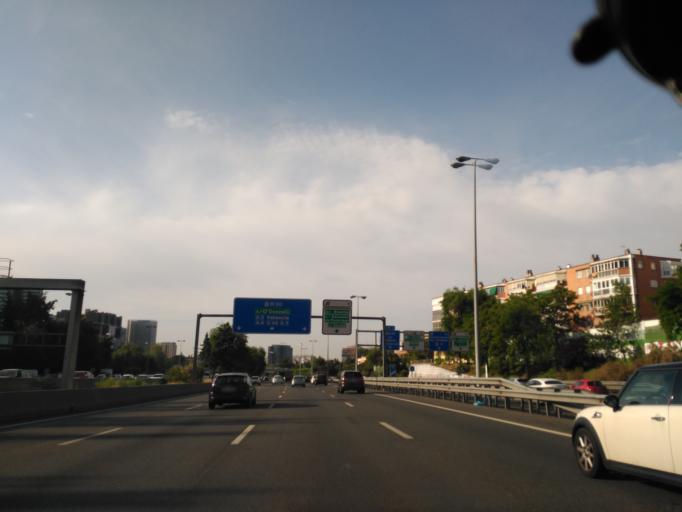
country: ES
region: Madrid
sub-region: Provincia de Madrid
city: Ciudad Lineal
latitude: 40.4486
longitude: -3.6624
